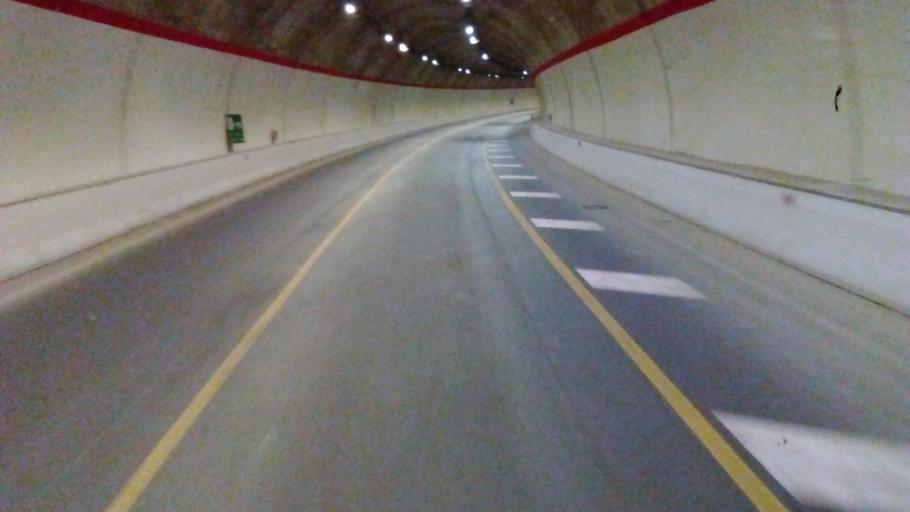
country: IT
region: Tuscany
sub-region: Provincia di Grosseto
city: Civitella Marittima
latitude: 43.0361
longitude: 11.2764
